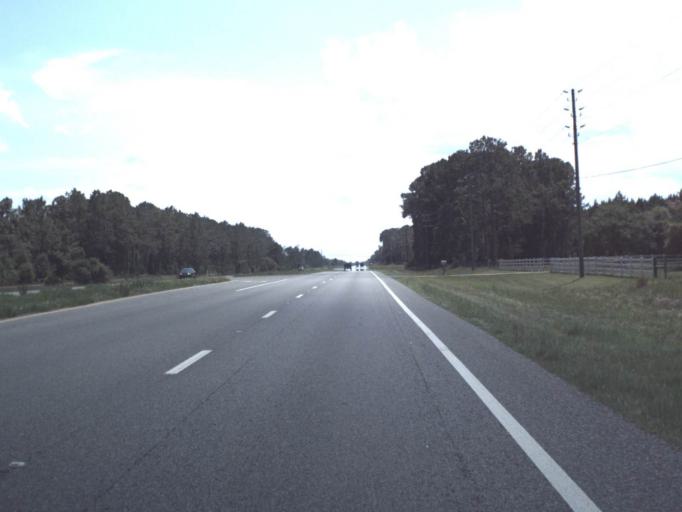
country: US
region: Florida
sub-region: Putnam County
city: Palatka
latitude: 29.7413
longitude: -81.6439
